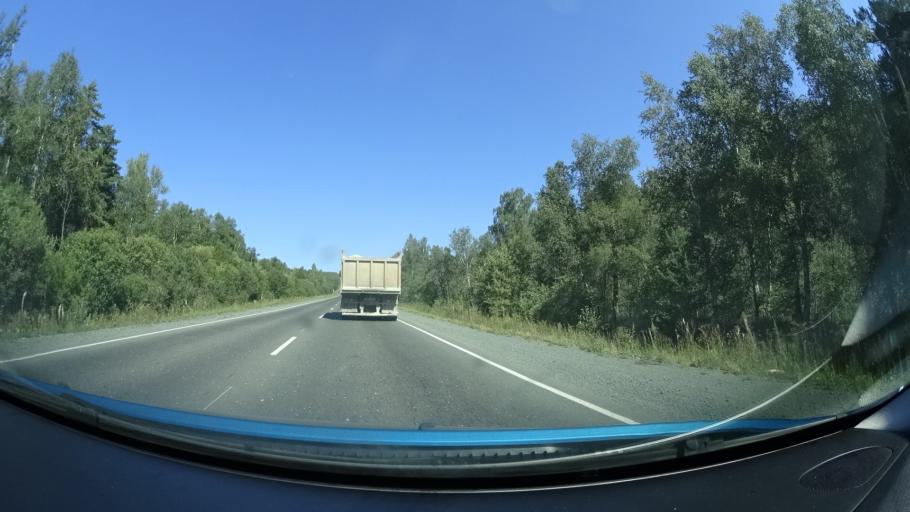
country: RU
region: Bashkortostan
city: Abzakovo
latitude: 53.8721
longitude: 58.5366
